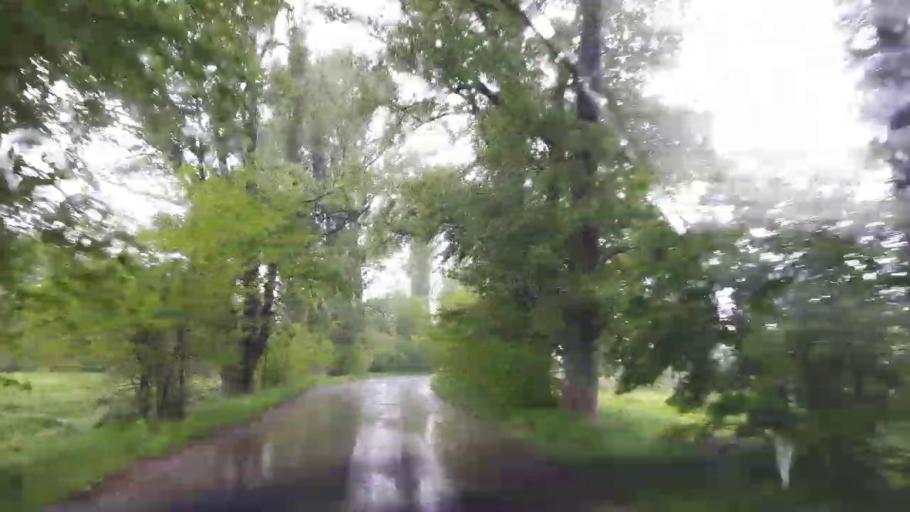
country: GE
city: Agara
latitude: 42.0113
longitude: 43.7769
